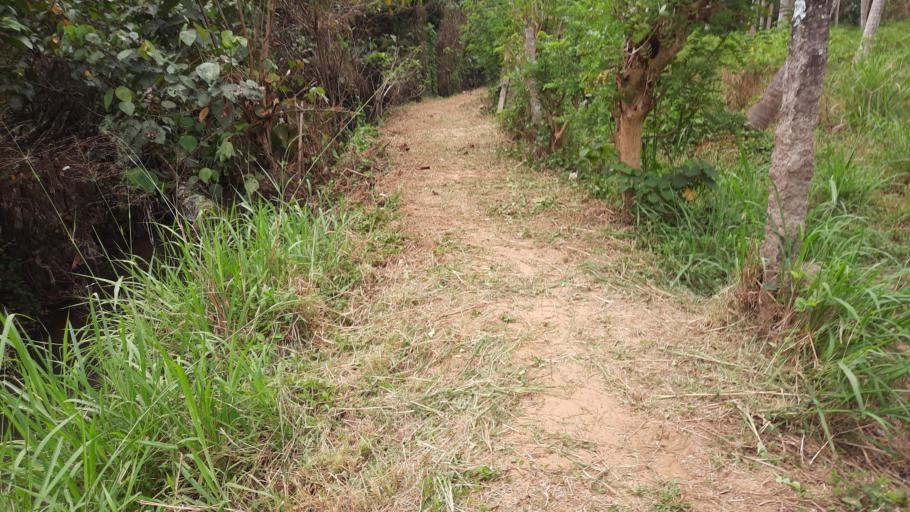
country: IN
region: Kerala
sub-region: Thiruvananthapuram
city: Thiruvananthapuram
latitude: 8.5596
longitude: 76.9332
